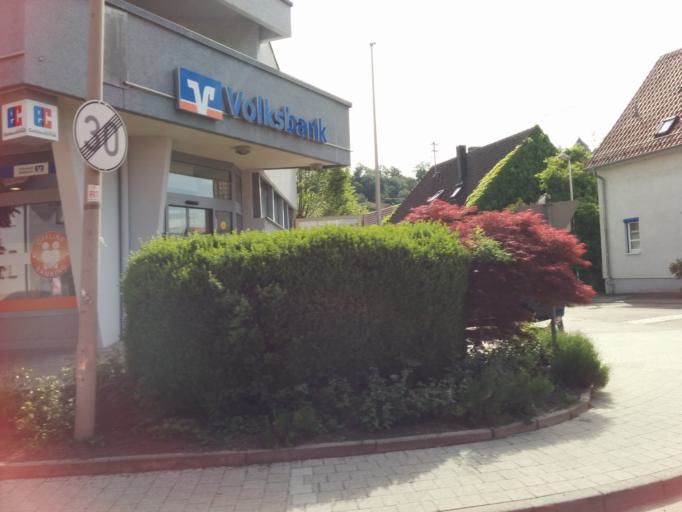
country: DE
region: Baden-Wuerttemberg
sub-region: Regierungsbezirk Stuttgart
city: Untergruppenbach
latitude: 49.0904
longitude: 9.2758
